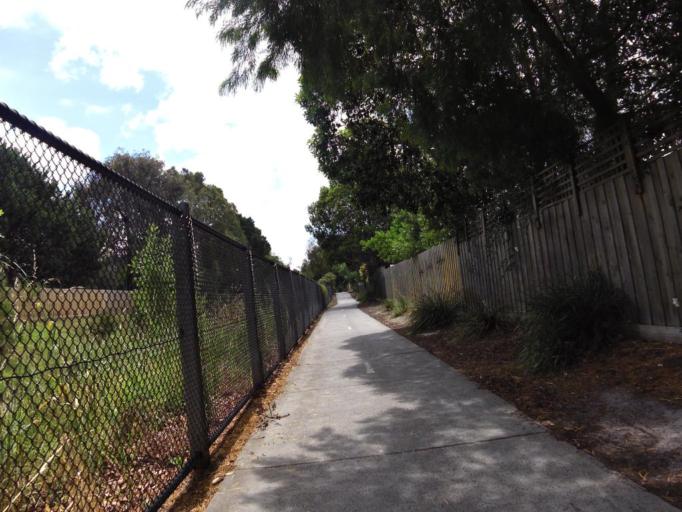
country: AU
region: Victoria
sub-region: Monash
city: Ashwood
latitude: -37.8618
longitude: 145.1013
